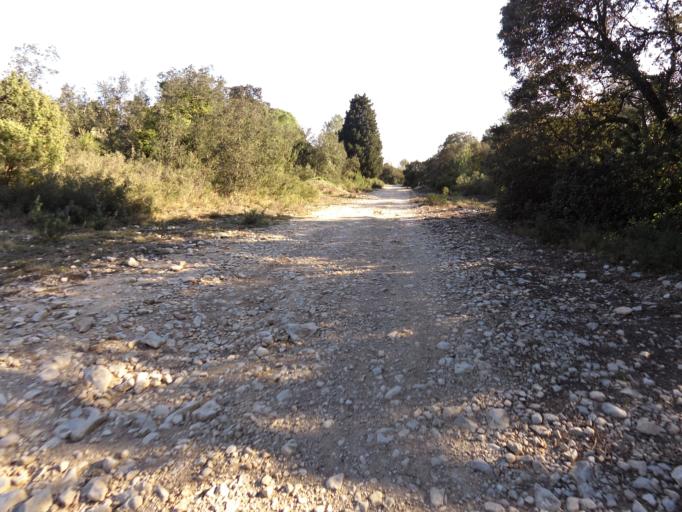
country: FR
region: Languedoc-Roussillon
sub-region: Departement du Gard
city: Congenies
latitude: 43.7588
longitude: 4.1771
